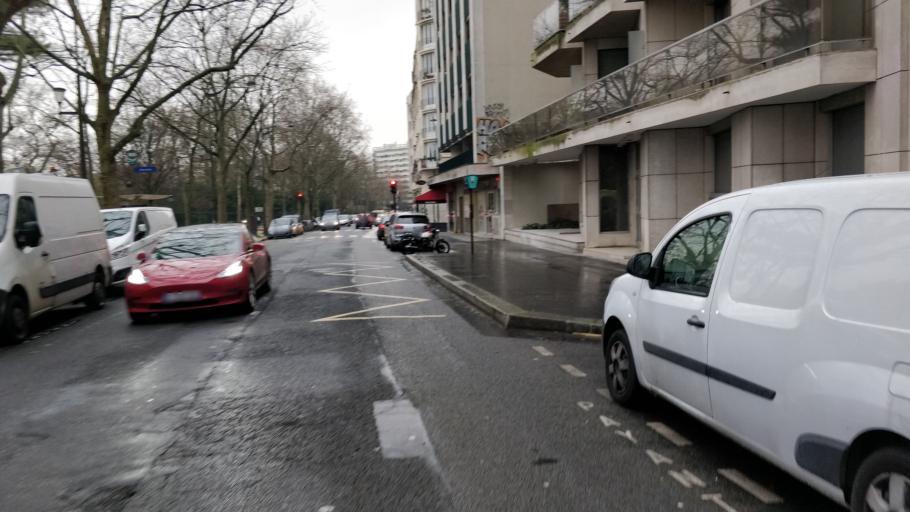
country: FR
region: Ile-de-France
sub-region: Departement de Seine-Saint-Denis
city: Le Pre-Saint-Gervais
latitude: 48.8794
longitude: 2.3850
